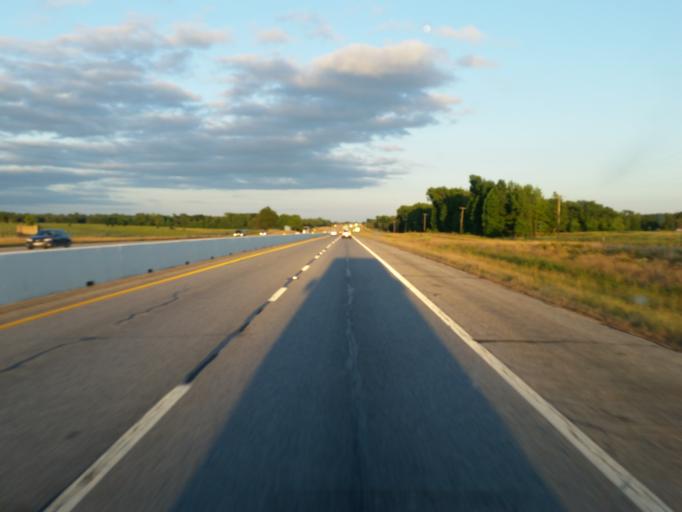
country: US
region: Texas
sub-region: Van Zandt County
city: Van
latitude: 32.5375
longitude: -95.7436
